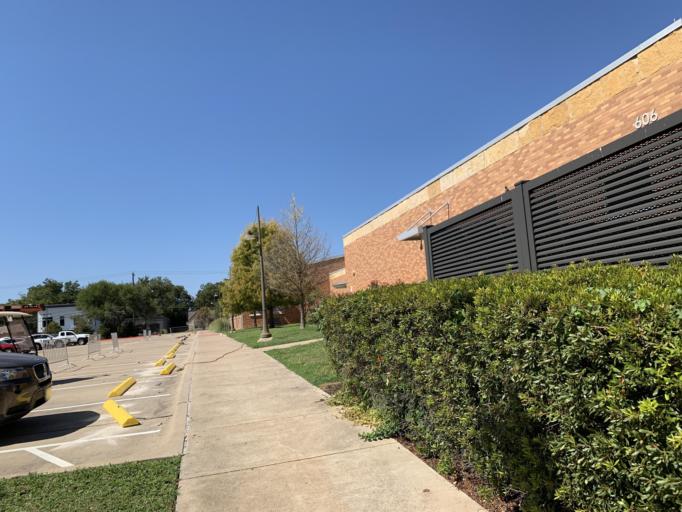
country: US
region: Texas
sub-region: Travis County
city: Austin
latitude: 30.3159
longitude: -97.7399
